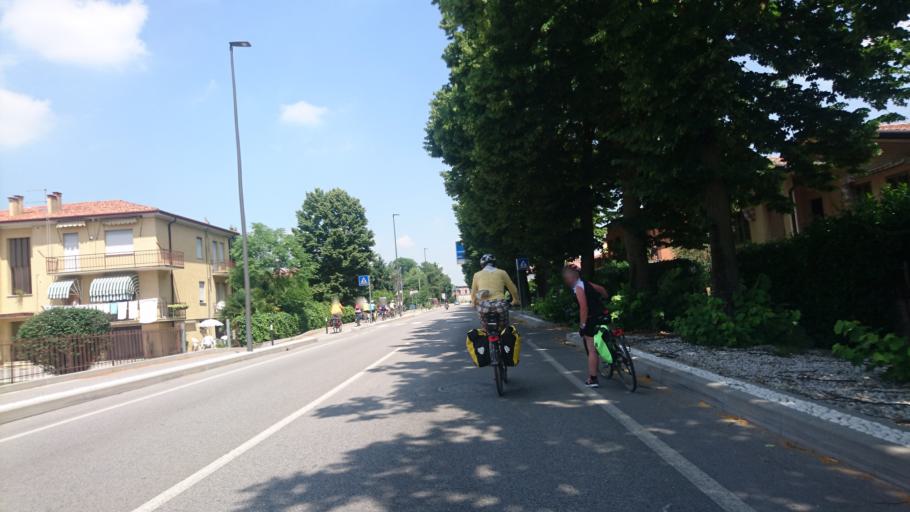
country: IT
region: Veneto
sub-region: Provincia di Venezia
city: Fiesso
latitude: 45.4160
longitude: 12.0525
